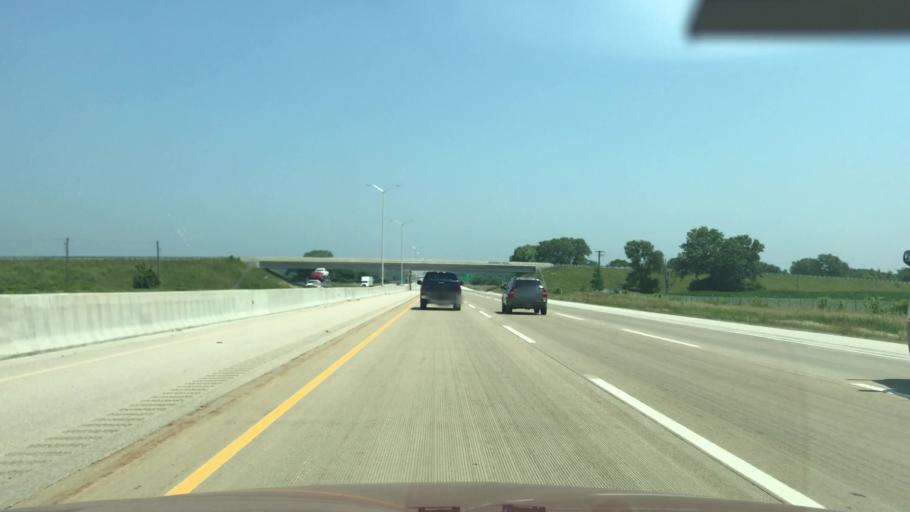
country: US
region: Illinois
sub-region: Kane County
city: Hampshire
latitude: 42.1514
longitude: -88.5379
